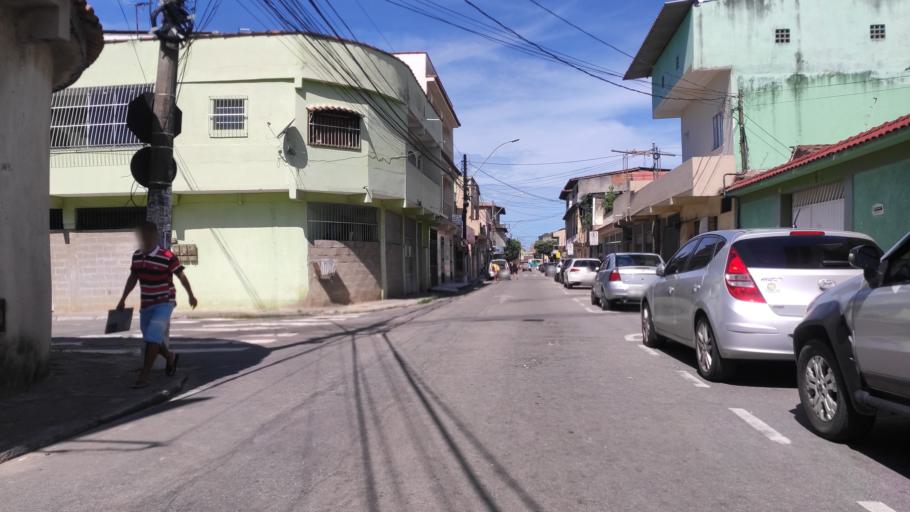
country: BR
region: Espirito Santo
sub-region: Serra
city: Serra
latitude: -20.1939
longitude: -40.2729
